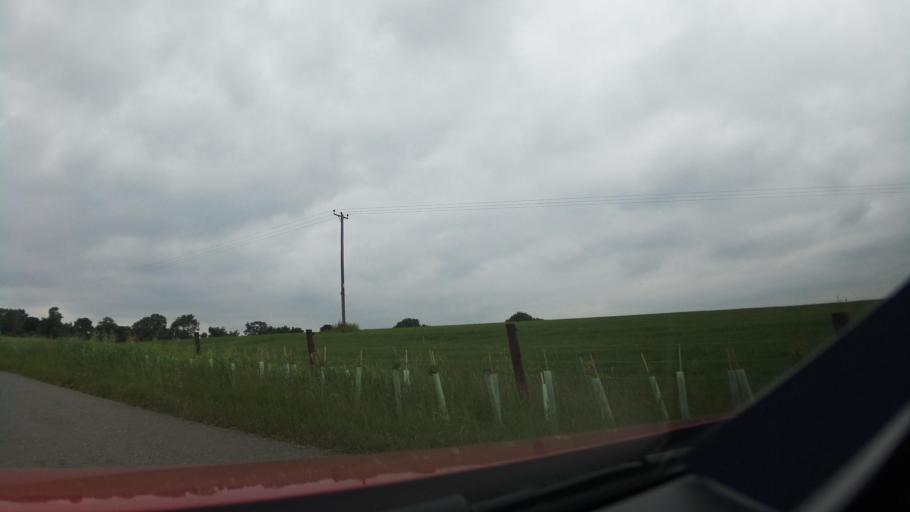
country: GB
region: England
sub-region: District of Rutland
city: Langham
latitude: 52.6781
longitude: -0.7943
